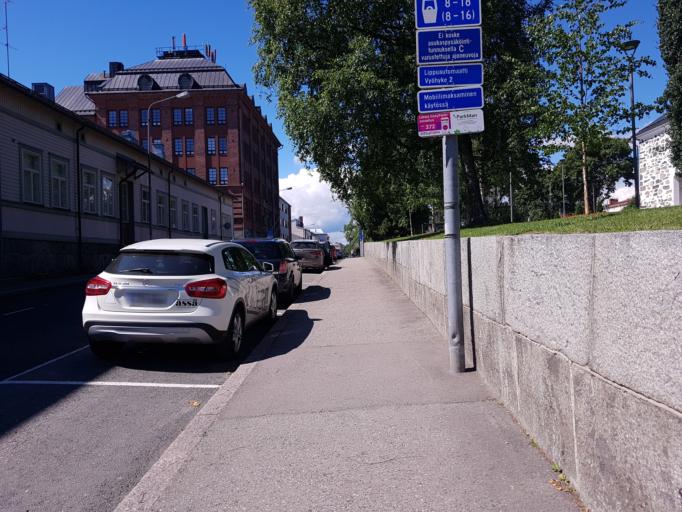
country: FI
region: Northern Savo
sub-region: Kuopio
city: Kuopio
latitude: 62.8909
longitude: 27.6853
